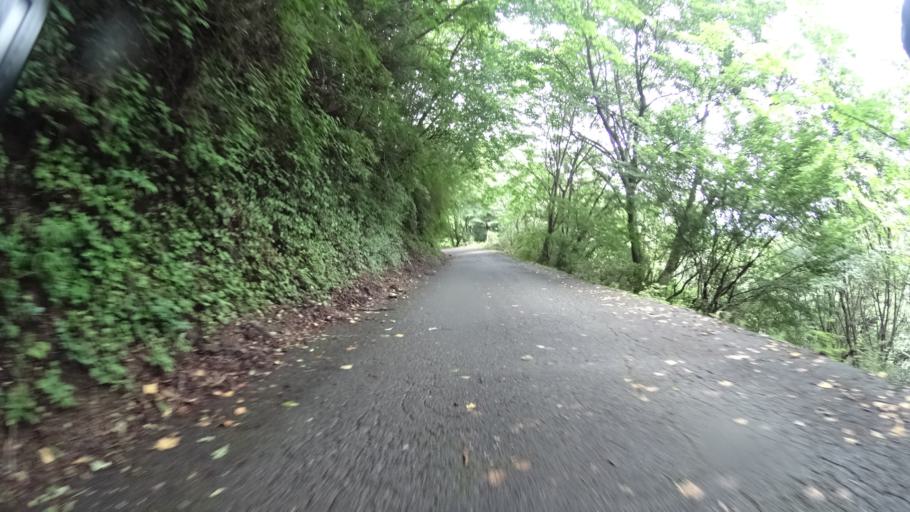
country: JP
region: Saitama
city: Chichibu
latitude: 35.8954
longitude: 139.1241
